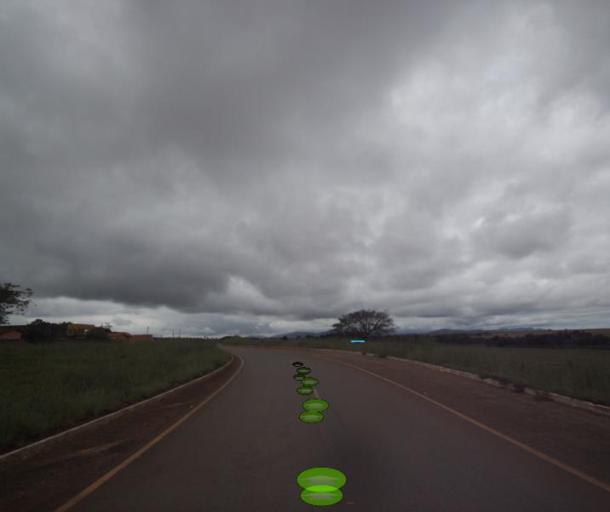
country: BR
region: Goias
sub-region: Barro Alto
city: Barro Alto
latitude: -14.8384
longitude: -49.0314
